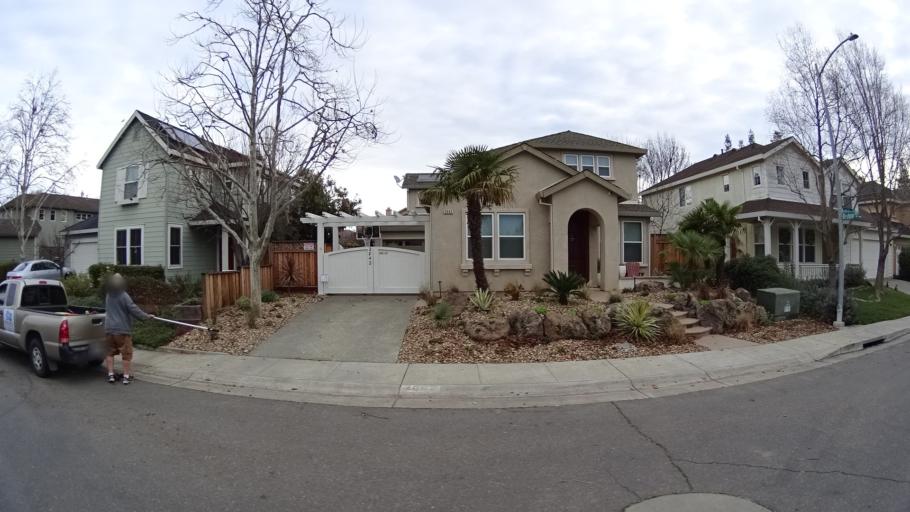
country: US
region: California
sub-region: Yolo County
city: Davis
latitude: 38.5700
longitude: -121.7257
